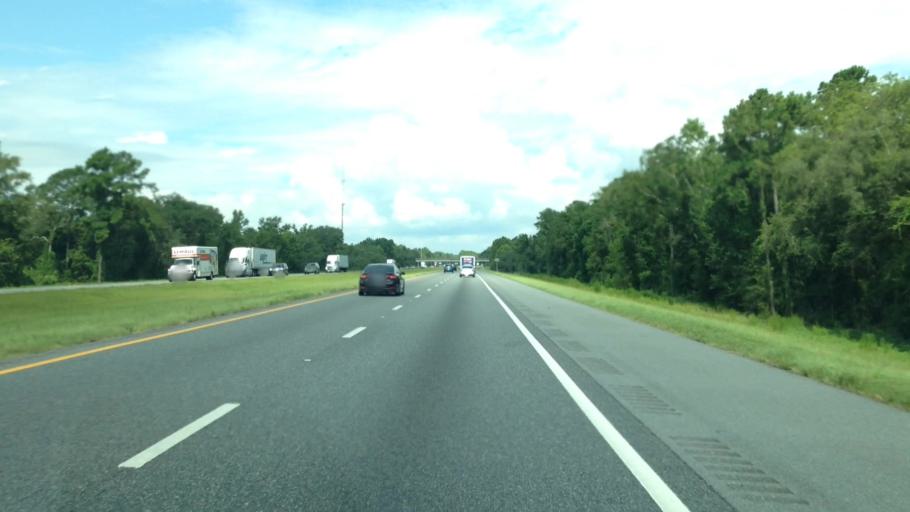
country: US
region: Florida
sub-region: Madison County
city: Madison
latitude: 30.3606
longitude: -83.2084
